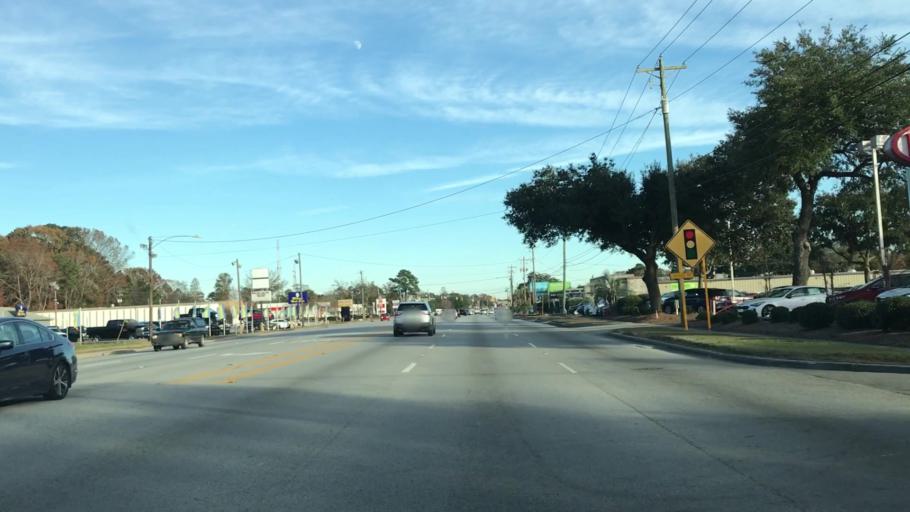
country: US
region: South Carolina
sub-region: Charleston County
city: Shell Point
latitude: 32.7924
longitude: -80.0464
